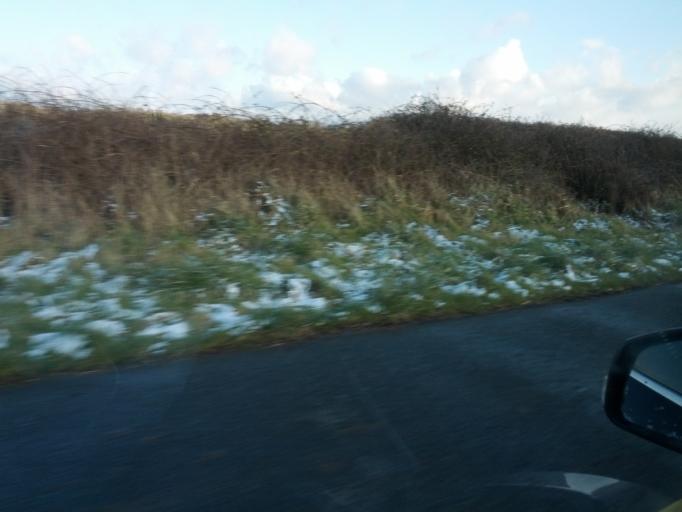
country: IE
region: Connaught
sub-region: County Galway
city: Gort
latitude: 53.1519
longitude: -8.8058
